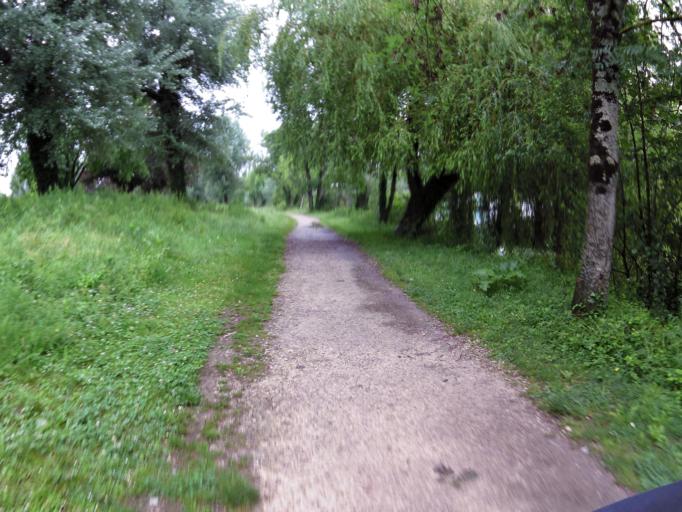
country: FR
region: Poitou-Charentes
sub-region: Departement de la Charente
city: Angouleme
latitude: 45.6597
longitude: 0.1594
